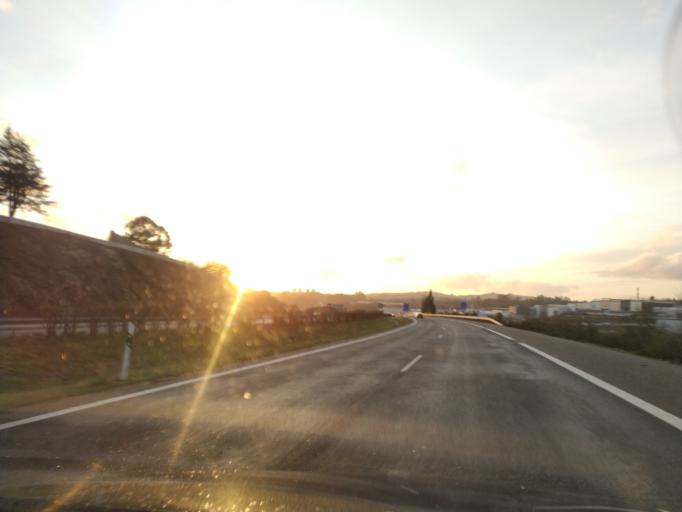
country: ES
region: Galicia
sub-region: Provincia da Coruna
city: Santiago de Compostela
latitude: 42.9012
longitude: -8.4959
